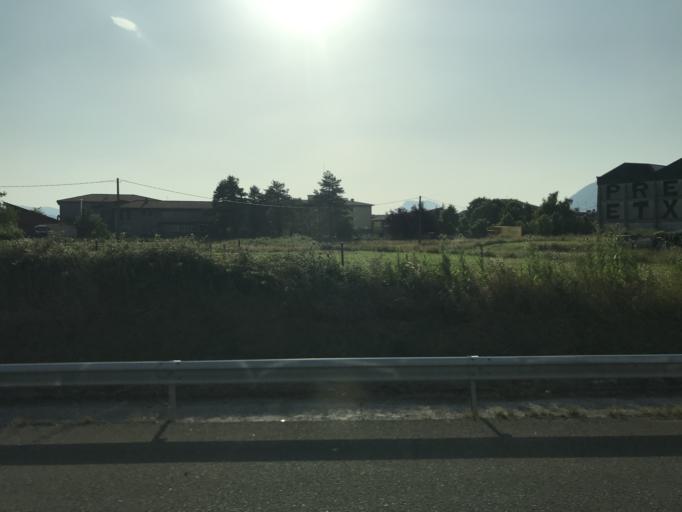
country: ES
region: Navarre
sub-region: Provincia de Navarra
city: Altsasu
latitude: 42.8993
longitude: -2.1754
